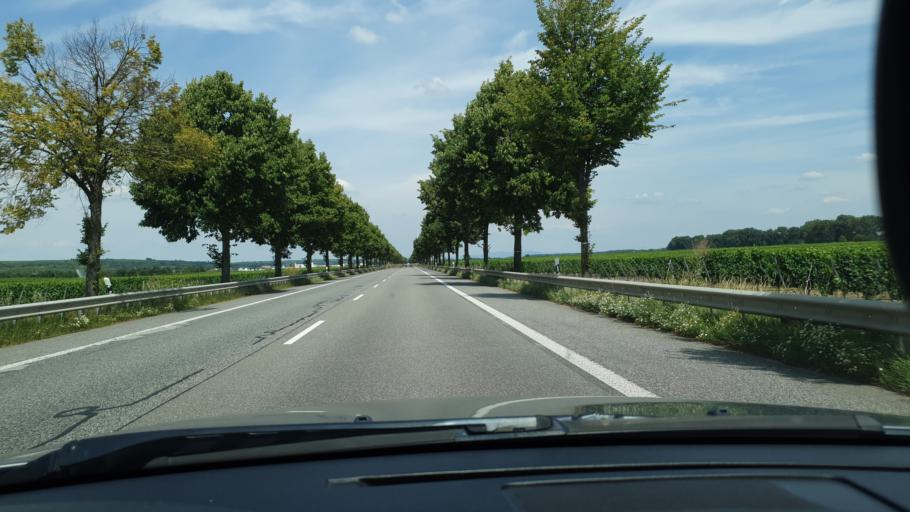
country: DE
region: Rheinland-Pfalz
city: Alsheim
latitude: 49.7545
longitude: 8.3523
